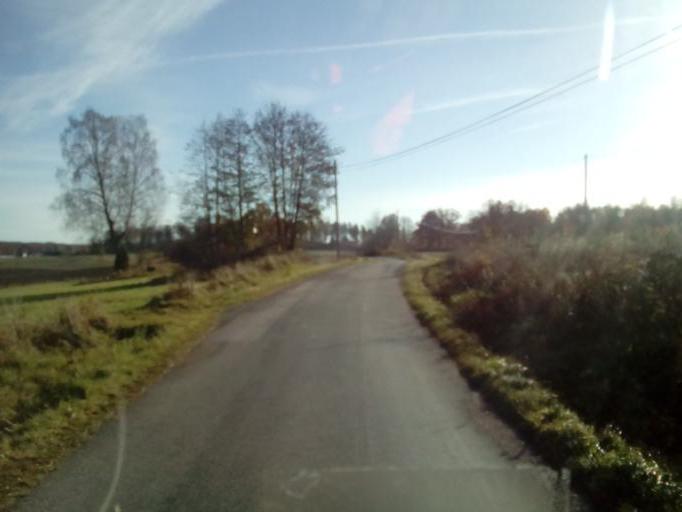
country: SE
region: Kalmar
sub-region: Vasterviks Kommun
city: Ankarsrum
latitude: 57.7979
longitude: 16.1846
